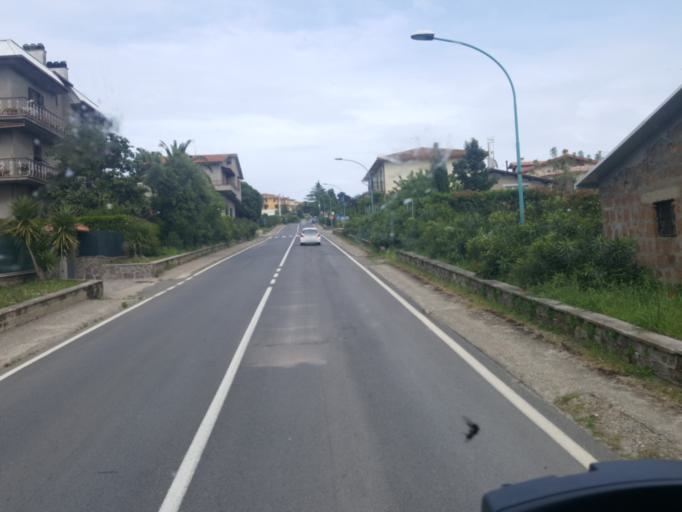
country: IT
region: Latium
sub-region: Provincia di Viterbo
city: Monte Romano
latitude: 42.2674
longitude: 11.8907
